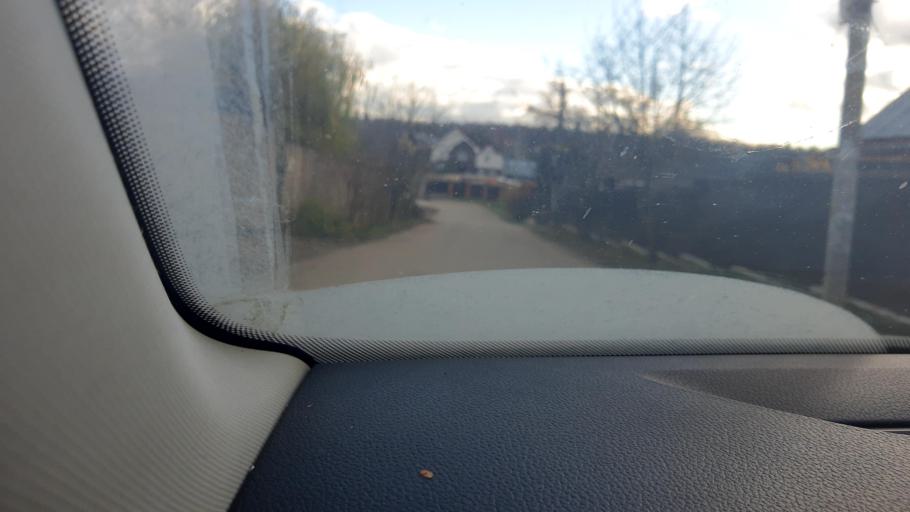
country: RU
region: Moscow
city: Annino
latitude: 55.5576
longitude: 37.6190
